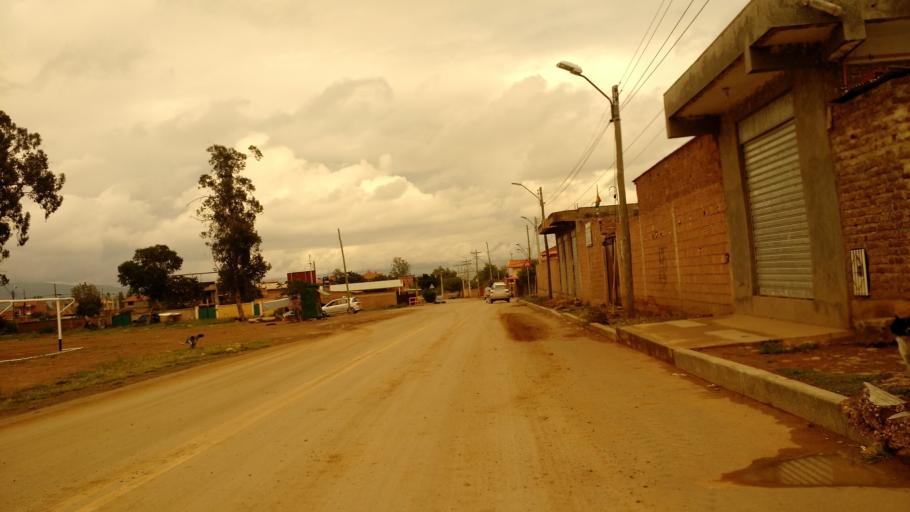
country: BO
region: Cochabamba
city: Cochabamba
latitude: -17.4497
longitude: -66.1519
